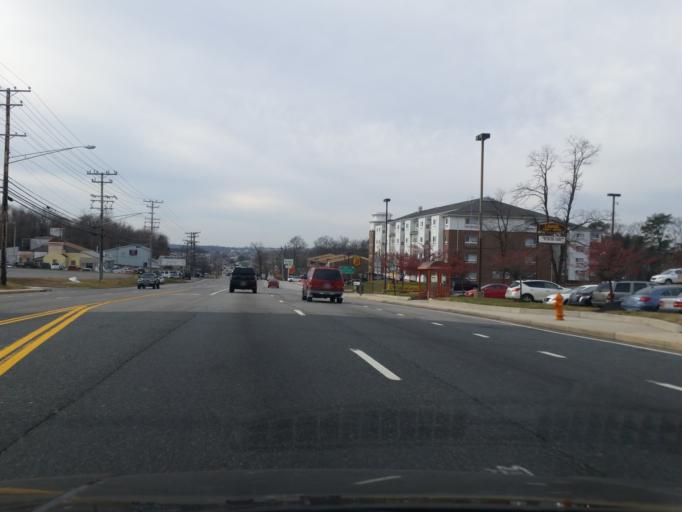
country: US
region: Maryland
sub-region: Prince George's County
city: Laurel
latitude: 39.1149
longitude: -76.8329
